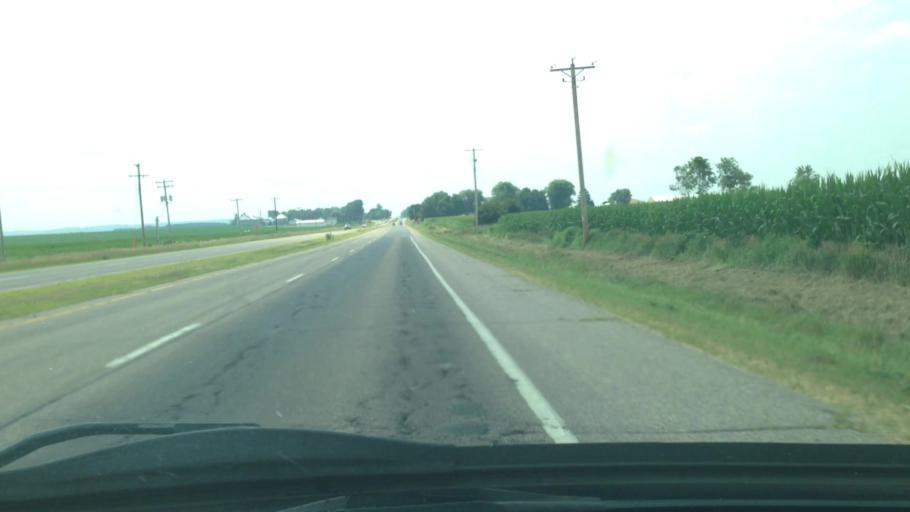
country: US
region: Wisconsin
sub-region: Sauk County
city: Prairie du Sac
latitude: 43.3269
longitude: -89.7591
